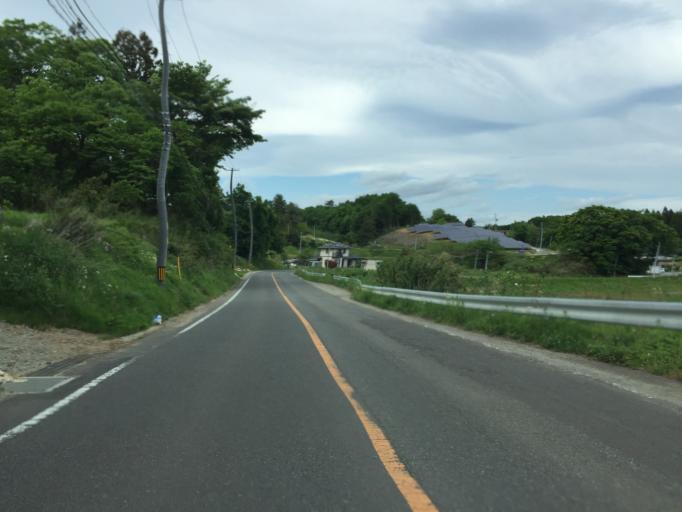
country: JP
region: Fukushima
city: Nihommatsu
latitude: 37.6350
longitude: 140.4927
